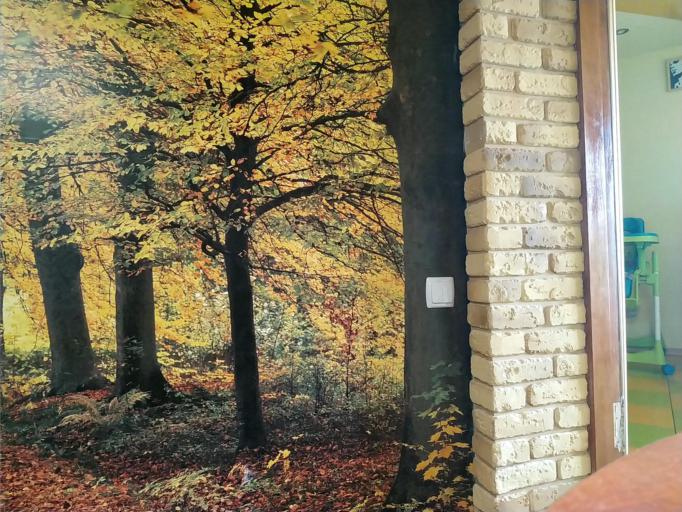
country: RU
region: Smolensk
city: Ozernyy
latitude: 55.4725
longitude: 32.6469
